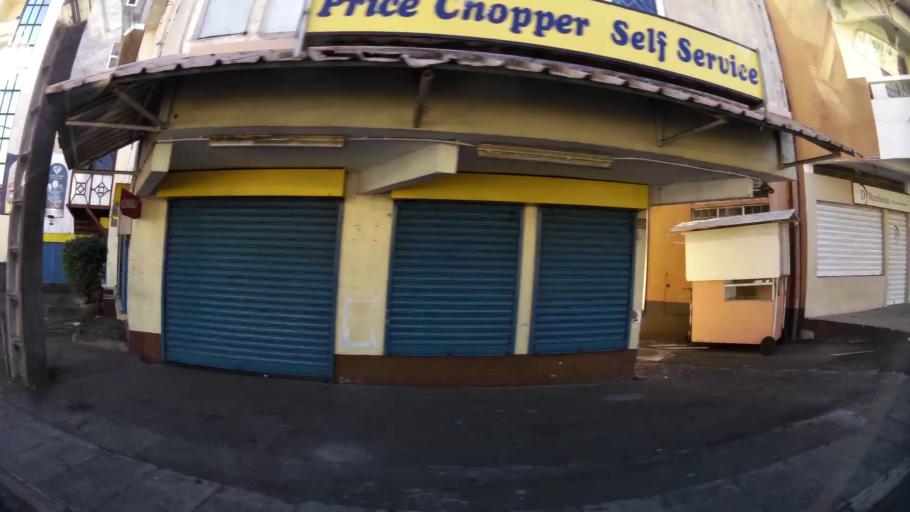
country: MU
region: Plaines Wilhems
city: Quatre Bornes
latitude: -20.2736
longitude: 57.4693
